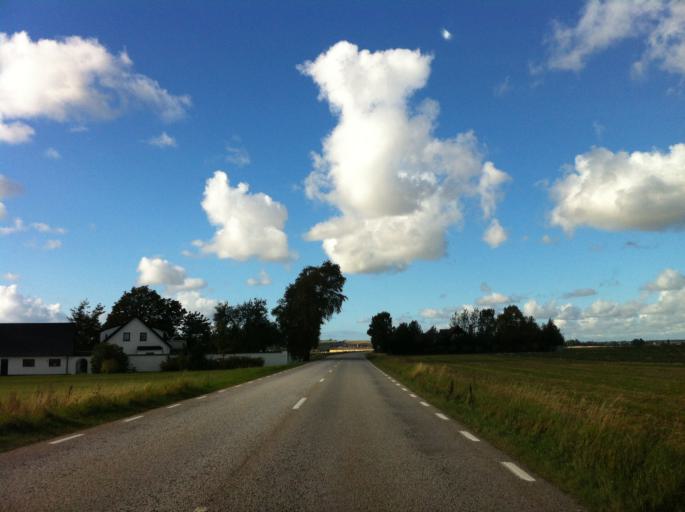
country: SE
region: Skane
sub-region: Landskrona
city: Asmundtorp
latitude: 55.8684
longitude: 12.9897
